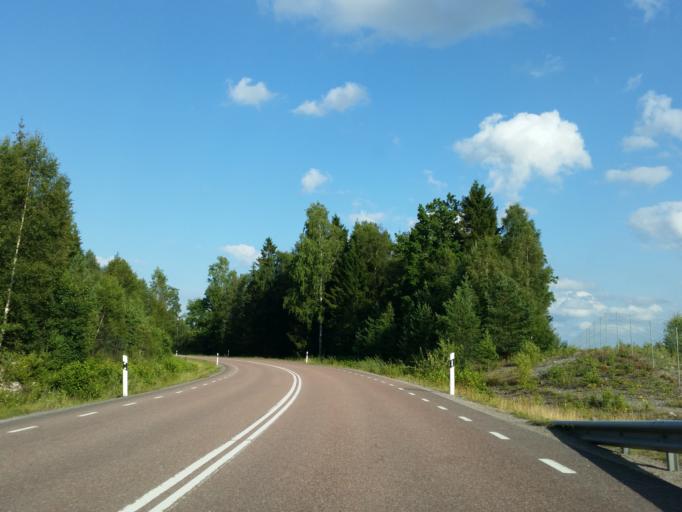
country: SE
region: Stockholm
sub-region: Nykvarns Kommun
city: Nykvarn
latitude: 59.2086
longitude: 17.3397
